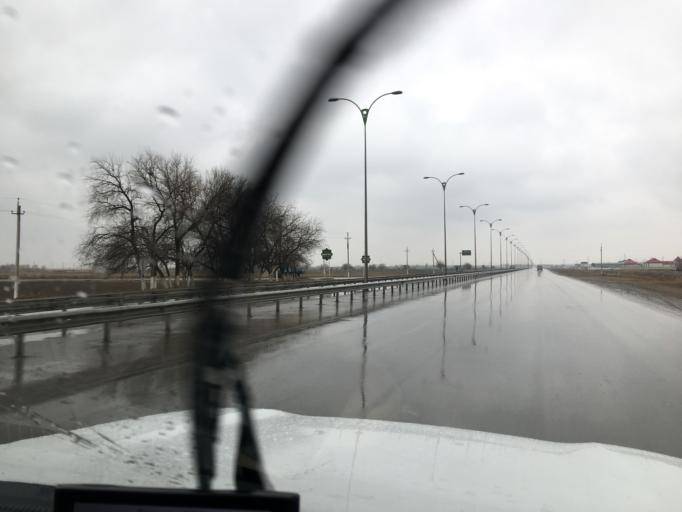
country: TM
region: Mary
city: Mary
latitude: 37.5564
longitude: 61.8553
